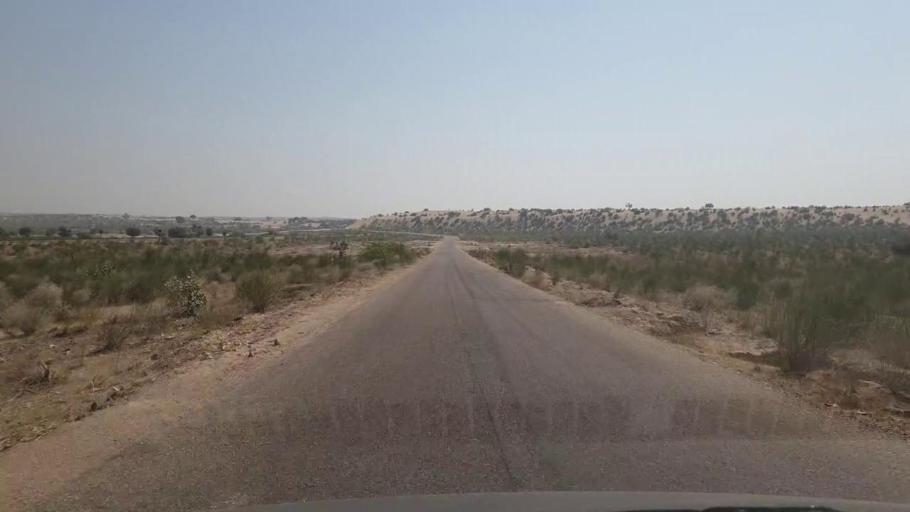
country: PK
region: Sindh
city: Chor
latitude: 25.6716
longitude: 70.1501
